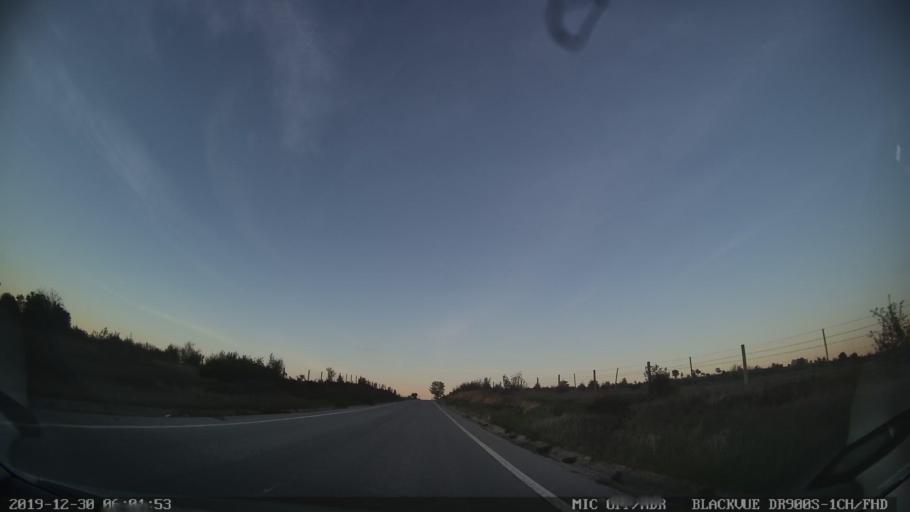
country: PT
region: Castelo Branco
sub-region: Penamacor
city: Penamacor
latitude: 40.0648
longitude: -7.2434
